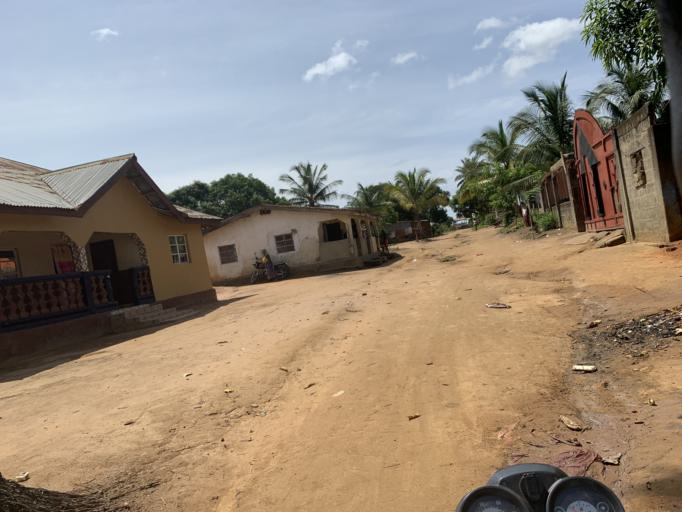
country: SL
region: Western Area
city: Waterloo
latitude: 8.3384
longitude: -13.0505
